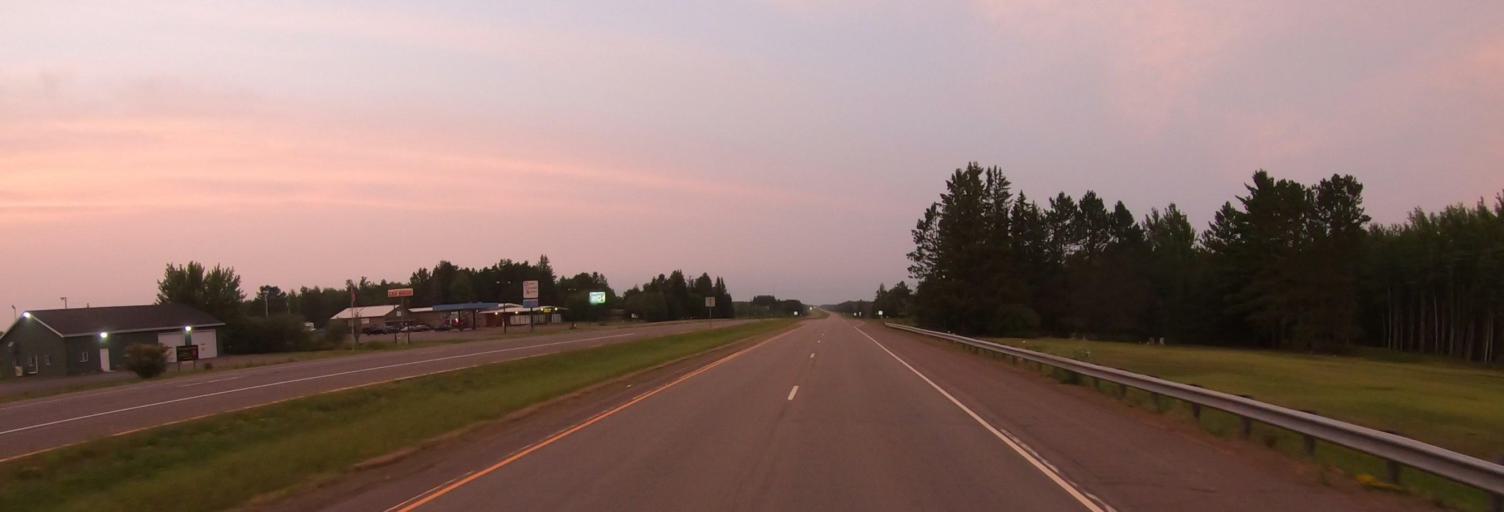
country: US
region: Minnesota
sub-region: Carlton County
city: Cloquet
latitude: 47.0365
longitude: -92.4711
